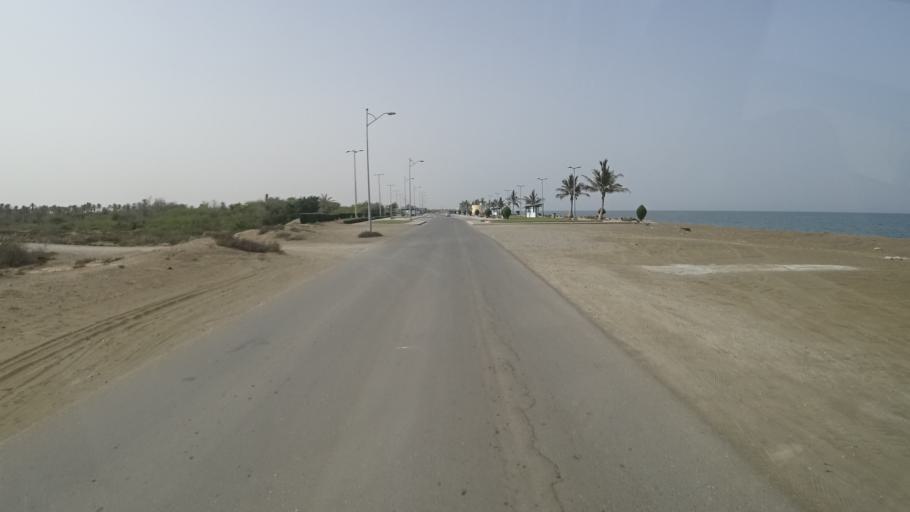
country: OM
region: Al Batinah
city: Saham
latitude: 24.2606
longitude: 56.8233
